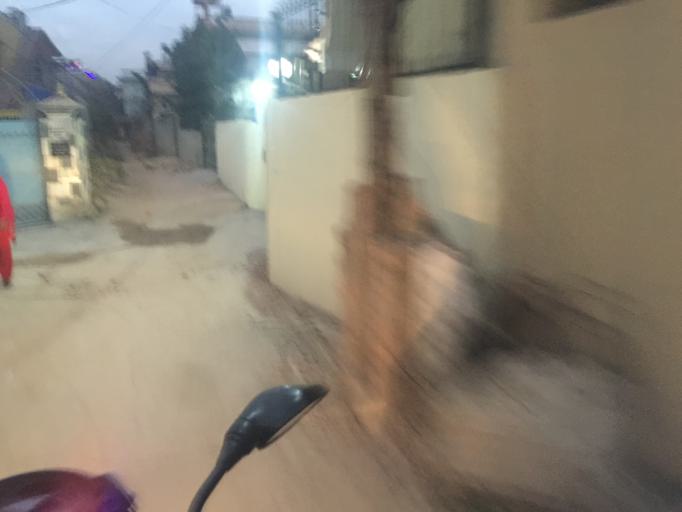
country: NP
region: Central Region
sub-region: Bagmati Zone
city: Patan
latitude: 27.6728
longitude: 85.3070
